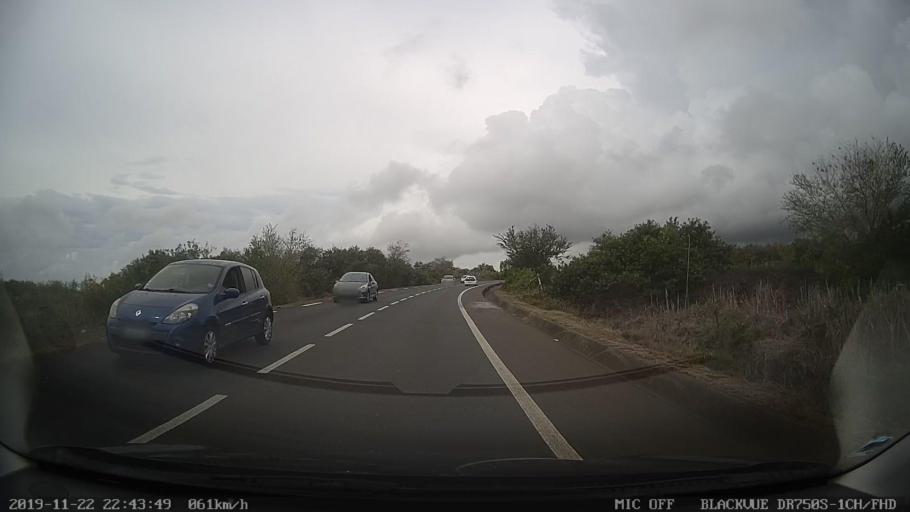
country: RE
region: Reunion
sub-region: Reunion
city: Saint-Paul
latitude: -21.0653
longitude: 55.2397
